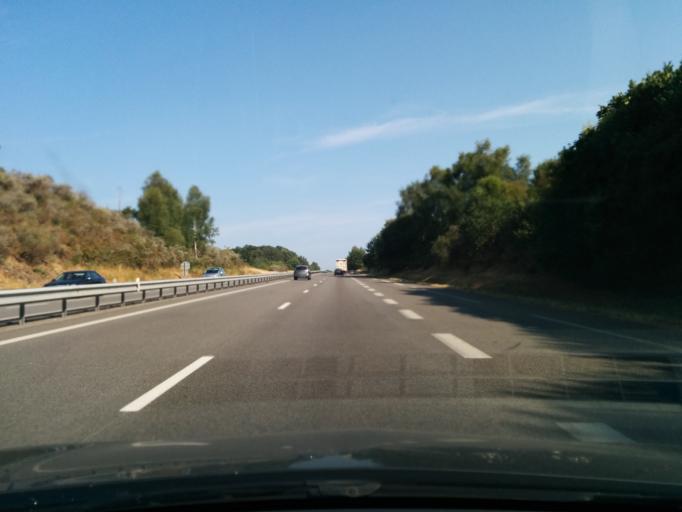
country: FR
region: Limousin
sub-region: Departement de la Haute-Vienne
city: Saint-Germain-les-Belles
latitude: 45.5822
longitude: 1.4767
